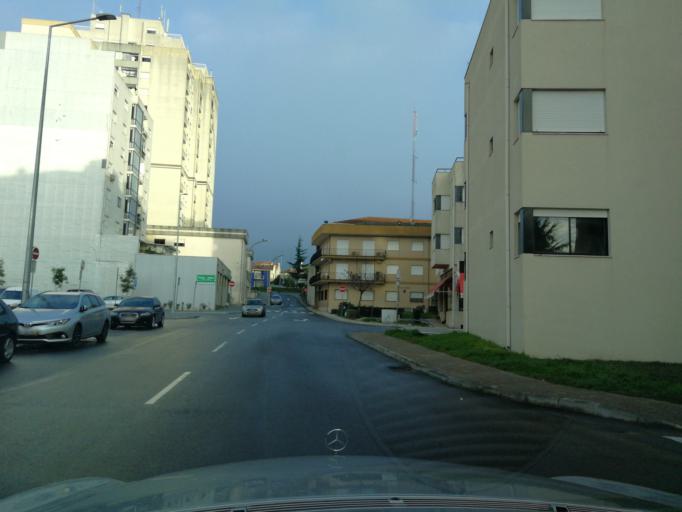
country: PT
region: Braga
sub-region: Braga
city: Braga
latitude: 41.5418
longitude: -8.4292
